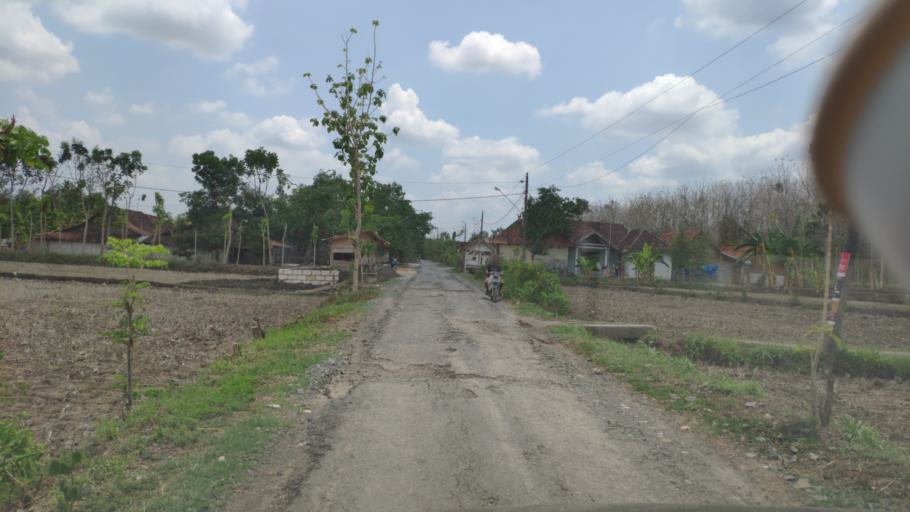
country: ID
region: Central Java
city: Gumiring
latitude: -7.0380
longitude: 111.3859
